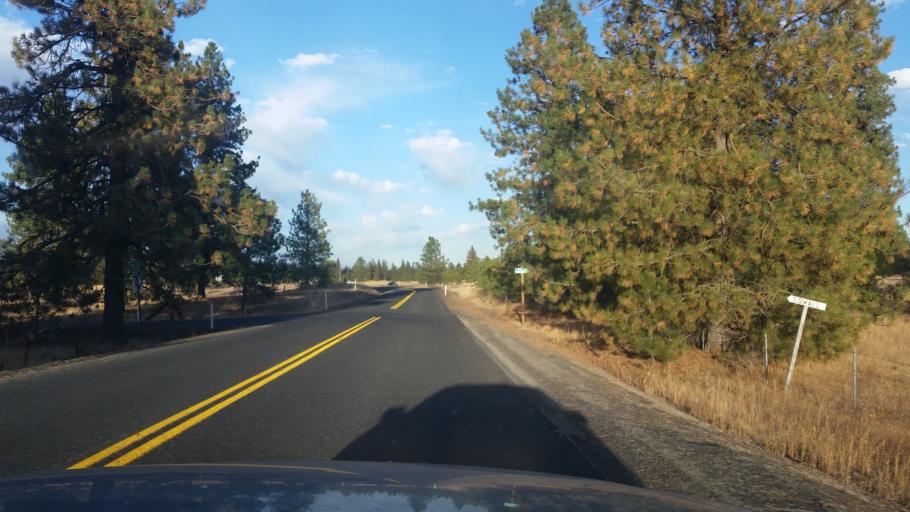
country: US
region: Washington
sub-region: Spokane County
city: Medical Lake
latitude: 47.4382
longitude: -117.7902
